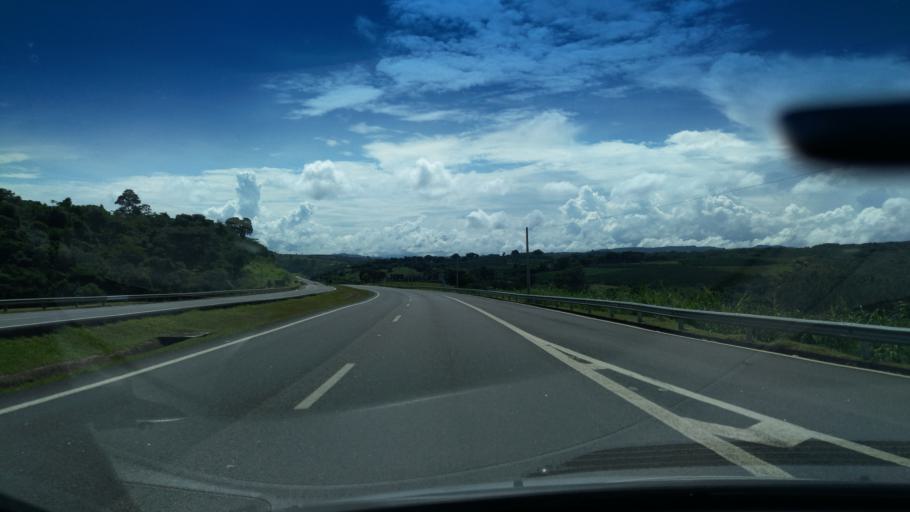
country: BR
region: Sao Paulo
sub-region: Santo Antonio Do Jardim
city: Espirito Santo do Pinhal
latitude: -22.2392
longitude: -46.8003
